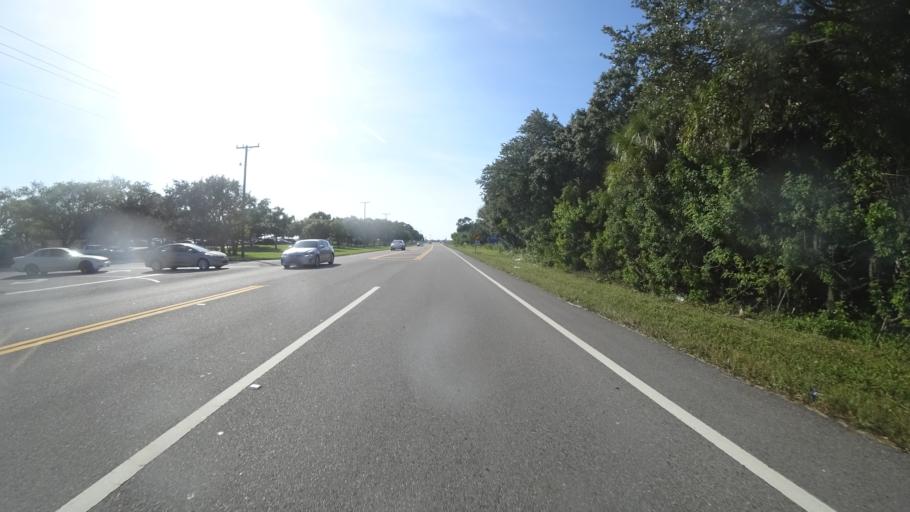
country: US
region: Florida
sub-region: Sarasota County
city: North Sarasota
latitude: 27.3890
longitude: -82.5399
